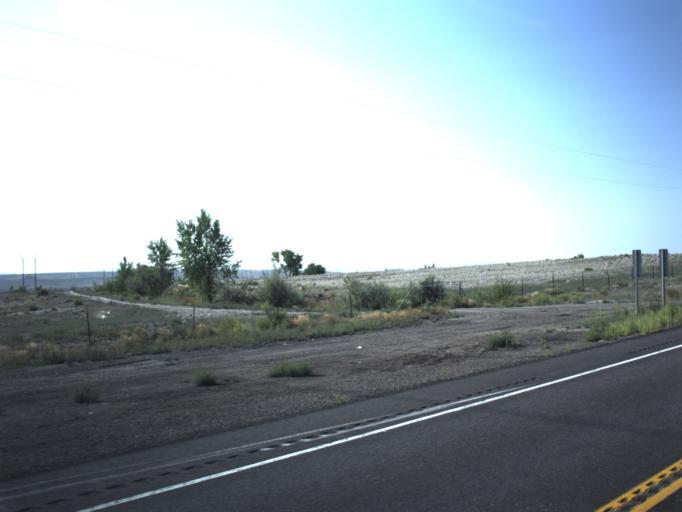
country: US
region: Utah
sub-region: Emery County
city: Castle Dale
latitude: 39.2606
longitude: -110.9827
